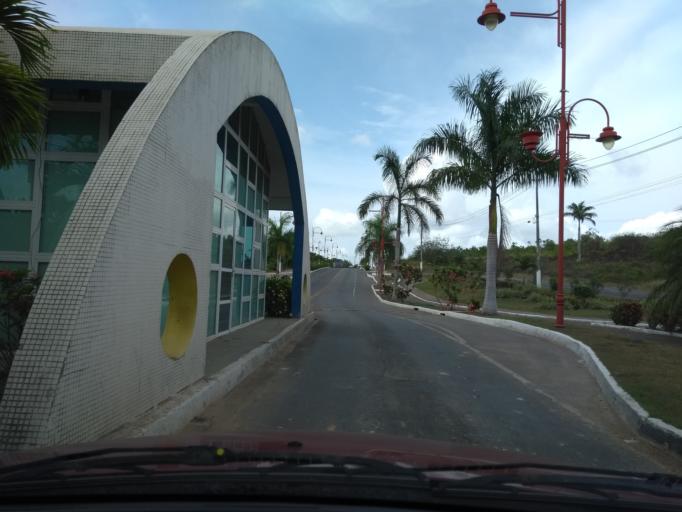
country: BR
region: Bahia
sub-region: Sao Francisco Do Conde
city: Sao Francisco do Conde
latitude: -12.6132
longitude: -38.6555
